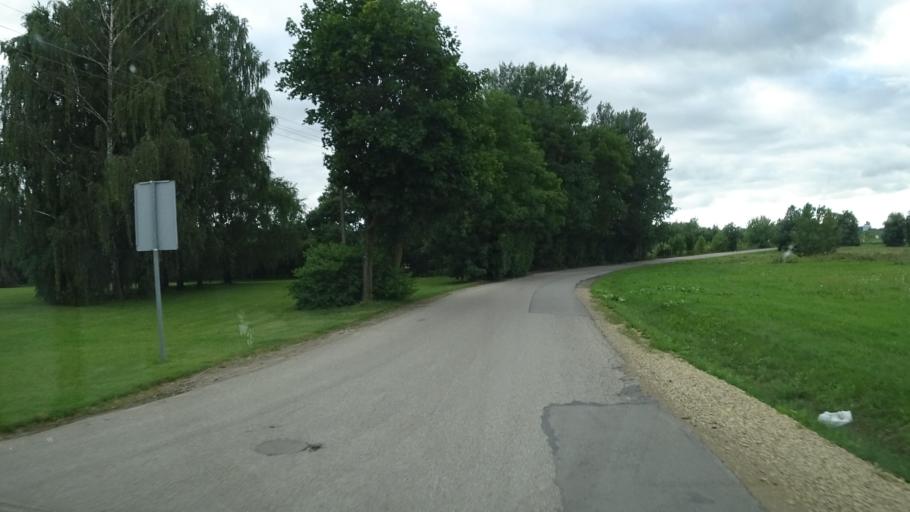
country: LT
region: Marijampoles apskritis
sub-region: Marijampole Municipality
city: Marijampole
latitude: 54.5821
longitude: 23.3645
